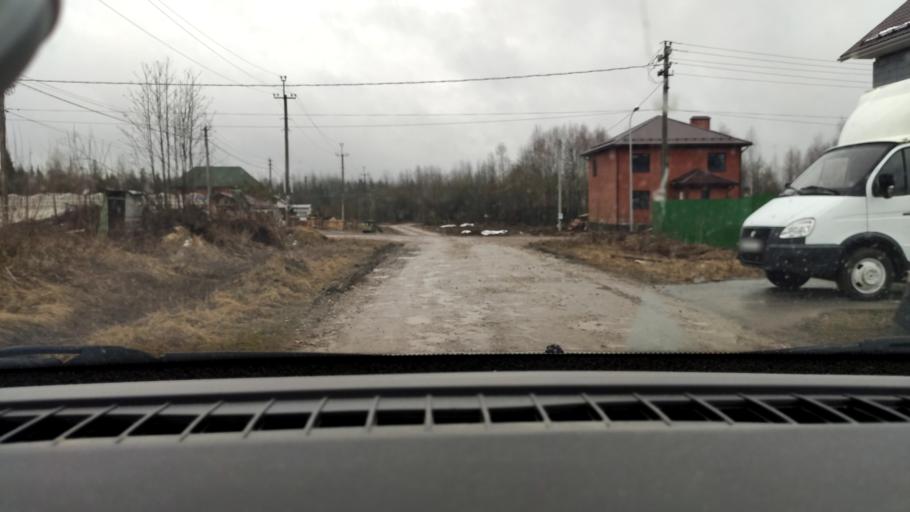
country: RU
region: Perm
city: Ferma
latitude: 57.9406
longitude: 56.4169
